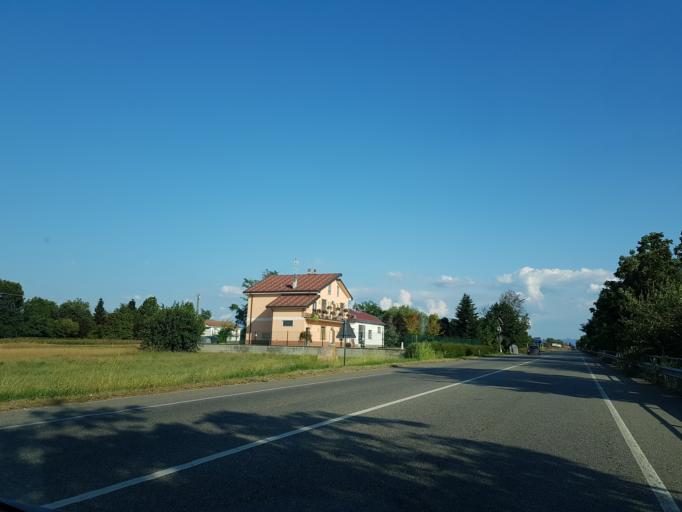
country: IT
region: Piedmont
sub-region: Provincia di Alessandria
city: Litta Parodi-Cascinagrossa
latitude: 44.8656
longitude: 8.7032
